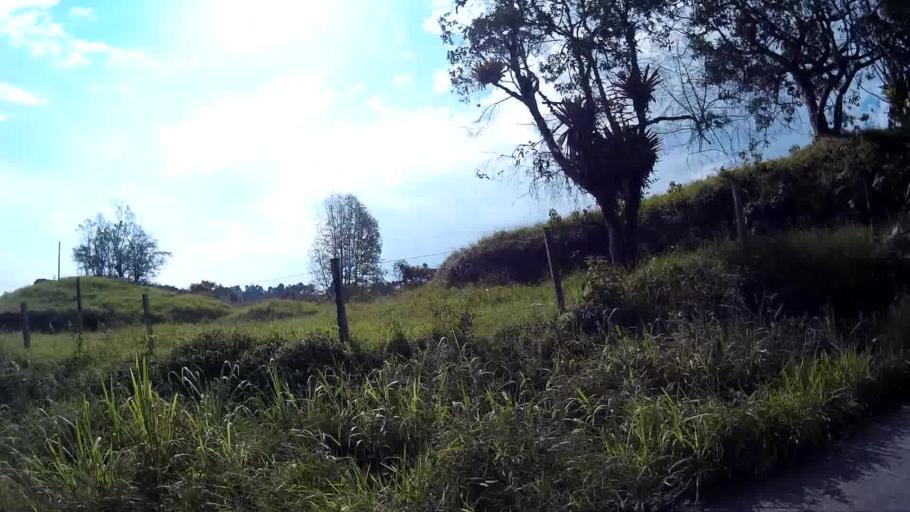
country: CO
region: Quindio
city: Filandia
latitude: 4.6860
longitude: -75.6351
